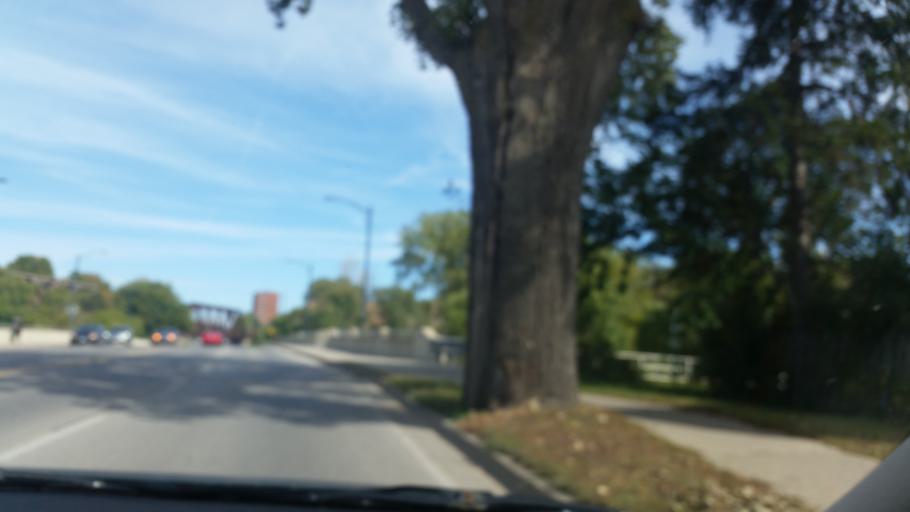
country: CA
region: Ontario
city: London
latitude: 42.9928
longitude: -81.2617
